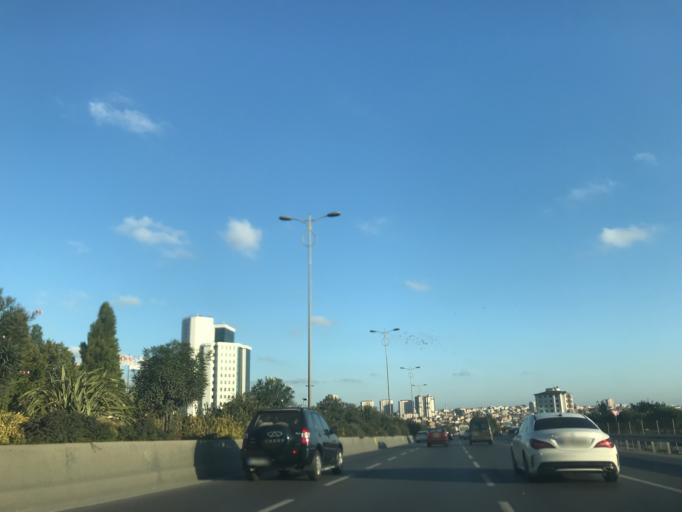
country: TR
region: Istanbul
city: Mahmutbey
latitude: 41.0601
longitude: 28.8430
